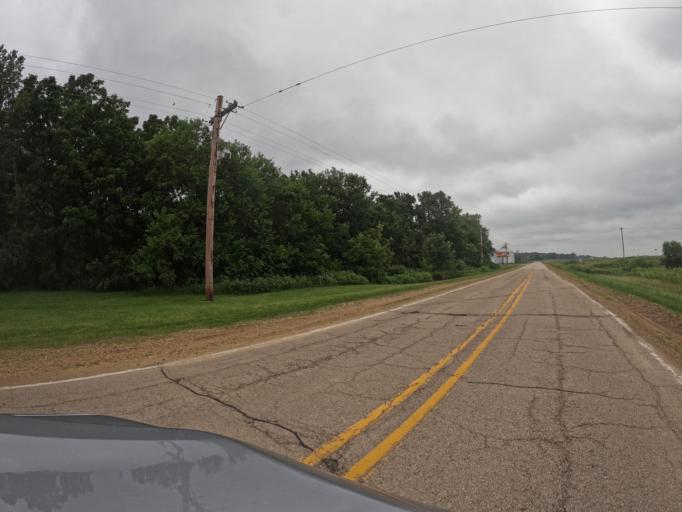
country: US
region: Iowa
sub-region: Clinton County
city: De Witt
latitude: 41.9117
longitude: -90.5969
